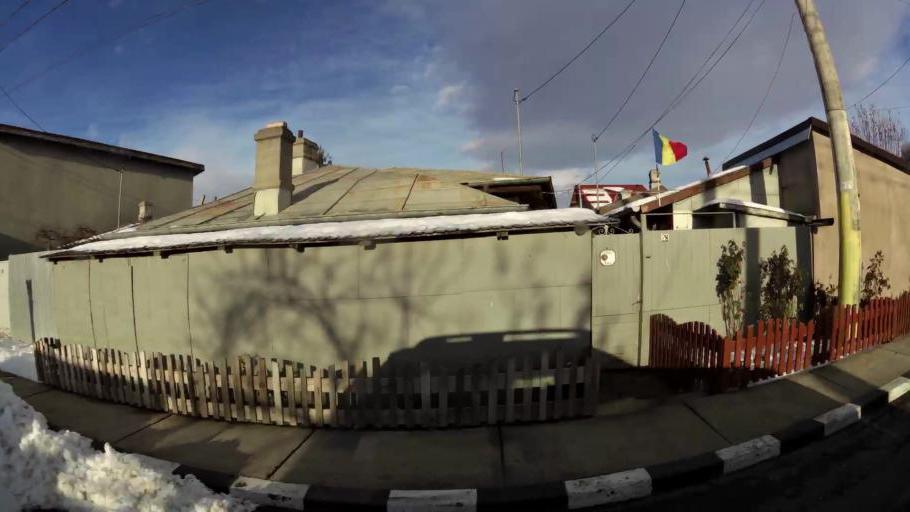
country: RO
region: Ilfov
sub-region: Comuna Fundeni-Dobroesti
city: Fundeni
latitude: 44.4626
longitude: 26.1653
